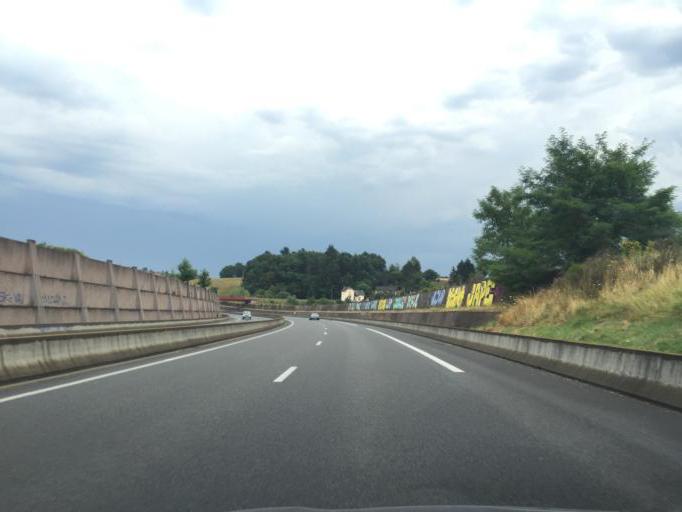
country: FR
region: Auvergne
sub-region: Departement de l'Allier
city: Lapalisse
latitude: 46.2366
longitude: 3.6276
